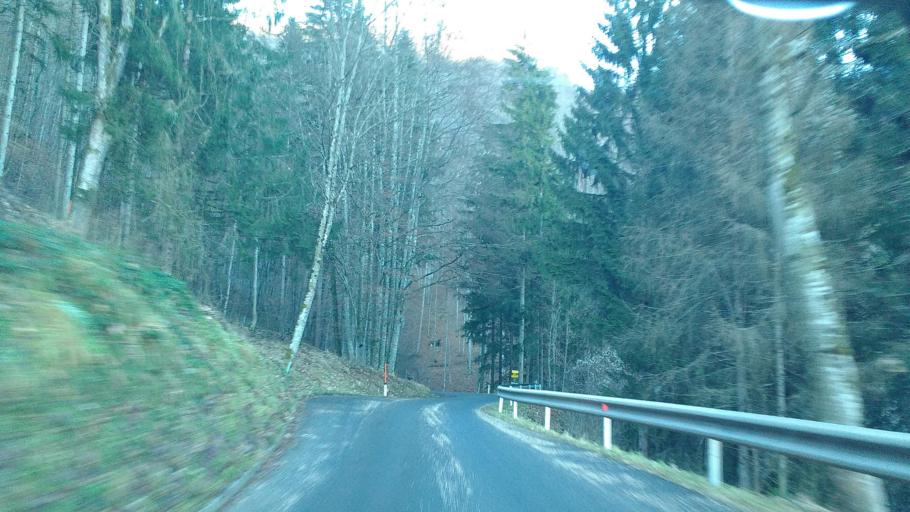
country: AT
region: Upper Austria
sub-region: Politischer Bezirk Kirchdorf an der Krems
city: Gruenburg
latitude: 47.8969
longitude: 14.2227
